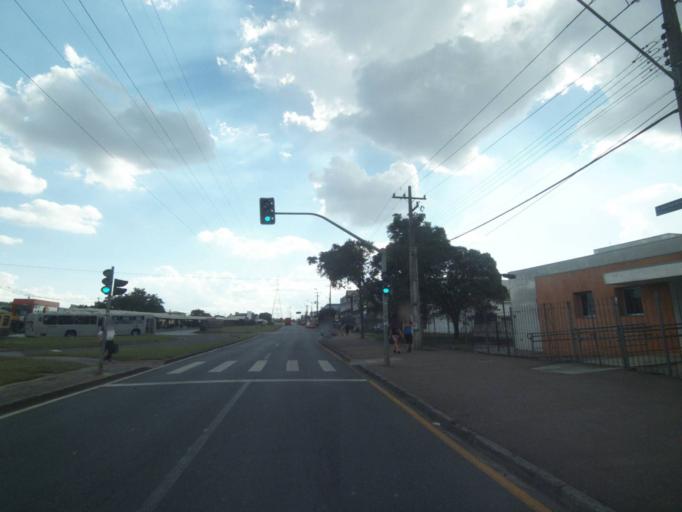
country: BR
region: Parana
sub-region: Sao Jose Dos Pinhais
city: Sao Jose dos Pinhais
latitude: -25.5338
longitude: -49.2667
